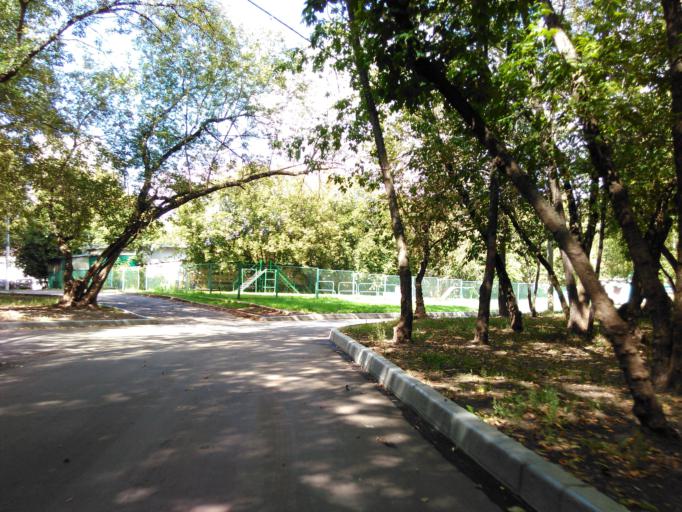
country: RU
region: Moscow
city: Novyye Cheremushki
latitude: 55.6930
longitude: 37.6137
